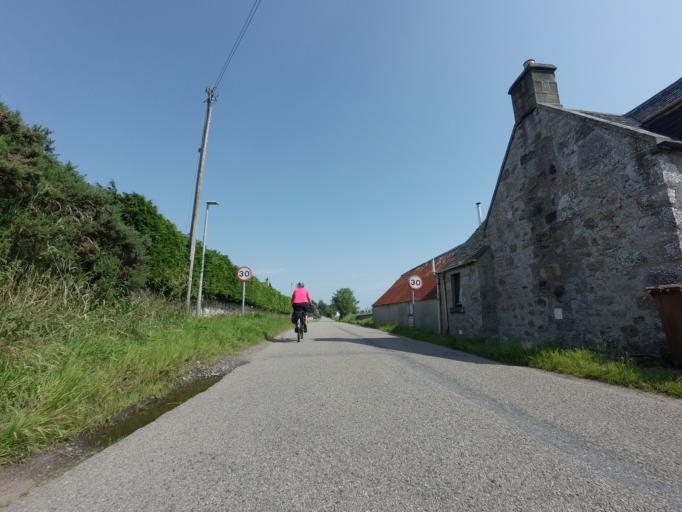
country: GB
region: Scotland
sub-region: Highland
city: Tain
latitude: 57.8017
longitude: -4.0666
